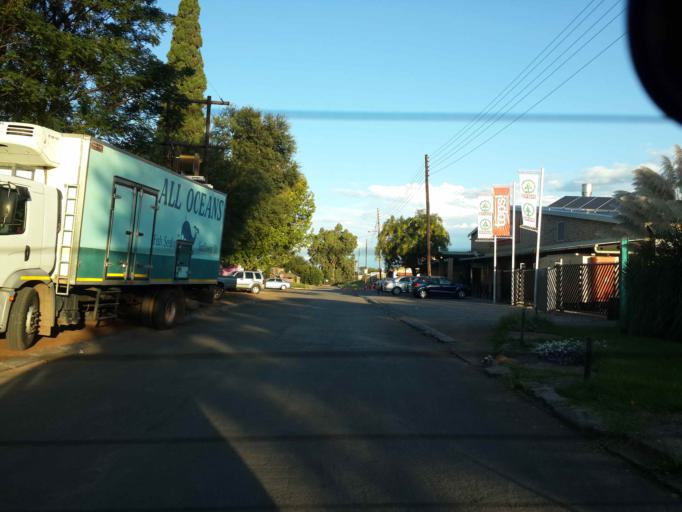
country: ZA
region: Northern Cape
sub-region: Siyanda District Municipality
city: Danielskuil
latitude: -28.1859
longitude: 23.5420
